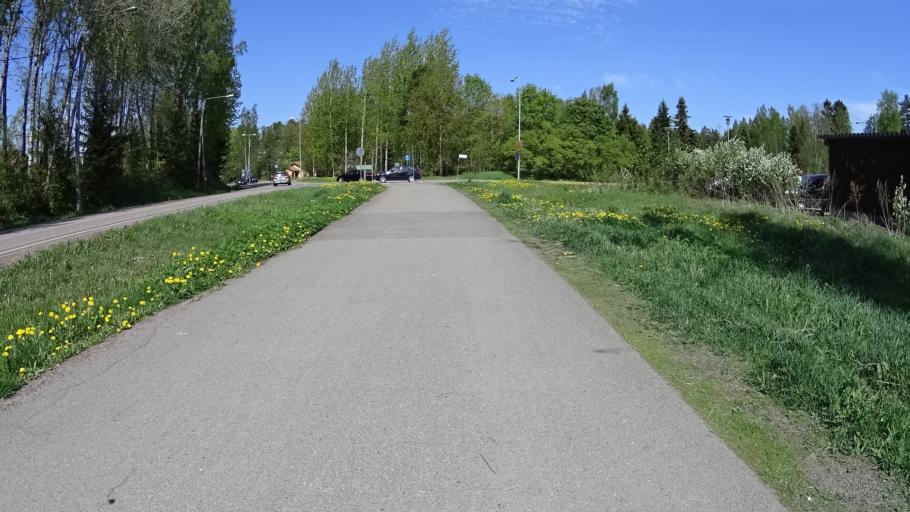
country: FI
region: Uusimaa
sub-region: Helsinki
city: Kauniainen
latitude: 60.2325
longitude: 24.7524
